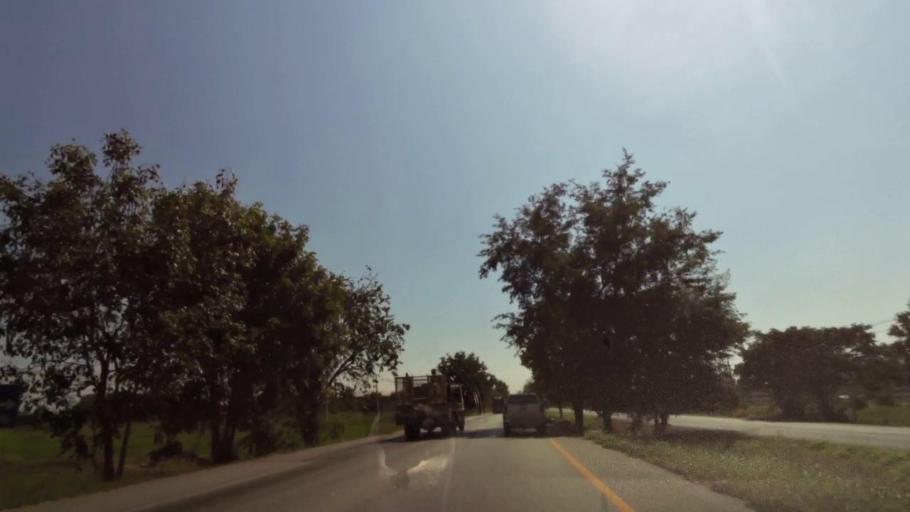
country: TH
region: Nakhon Sawan
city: Kao Liao
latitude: 15.8182
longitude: 100.1196
